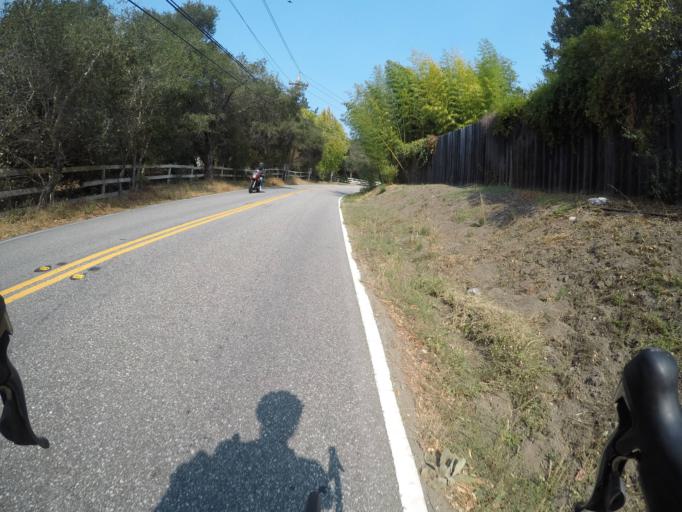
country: US
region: California
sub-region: Santa Cruz County
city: Pasatiempo
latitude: 37.0243
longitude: -122.0213
